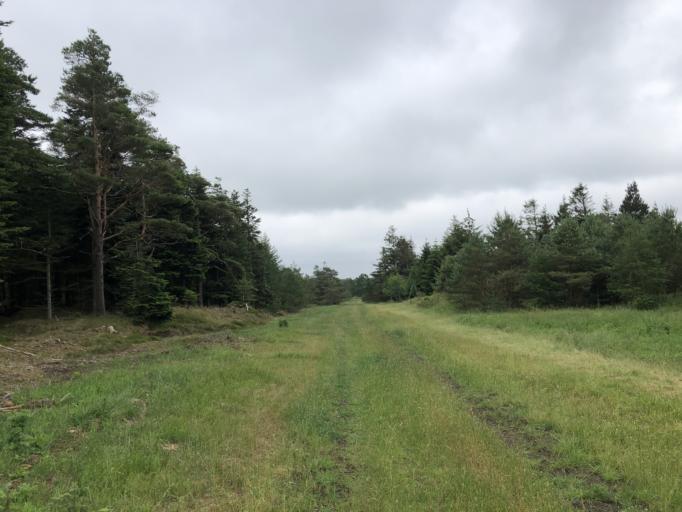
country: DK
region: Central Jutland
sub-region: Holstebro Kommune
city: Ulfborg
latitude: 56.2502
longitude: 8.3612
